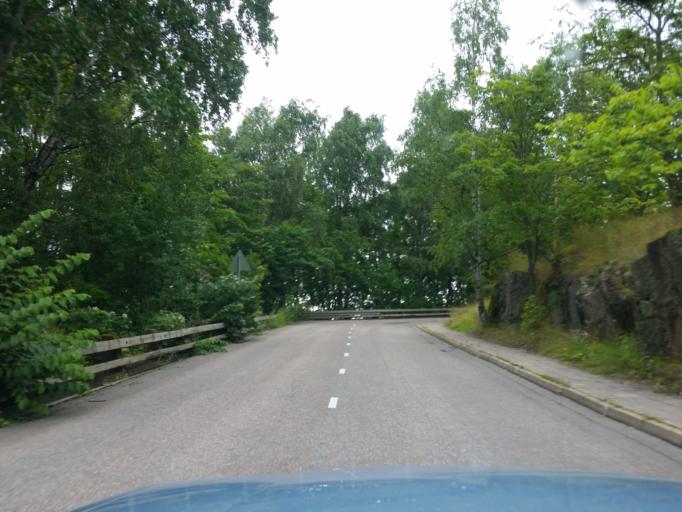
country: FI
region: Varsinais-Suomi
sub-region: Turku
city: Turku
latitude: 60.4554
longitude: 22.2827
